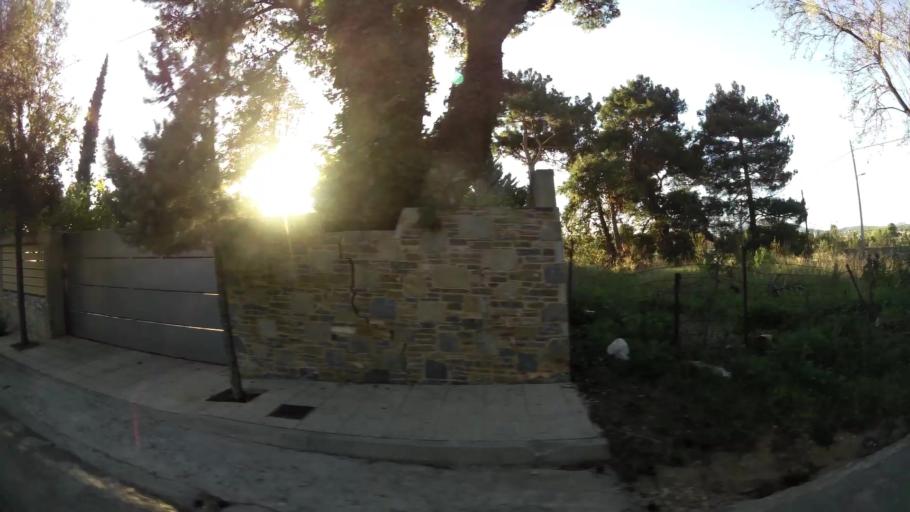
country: GR
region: Attica
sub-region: Nomarchia Anatolikis Attikis
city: Kryoneri
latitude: 38.1292
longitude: 23.8307
